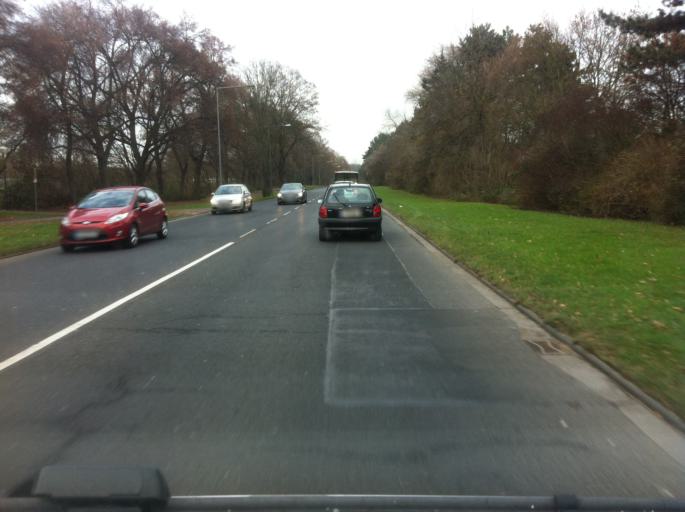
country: DE
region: North Rhine-Westphalia
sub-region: Regierungsbezirk Koln
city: Bilderstoeckchen
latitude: 50.9731
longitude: 6.9128
